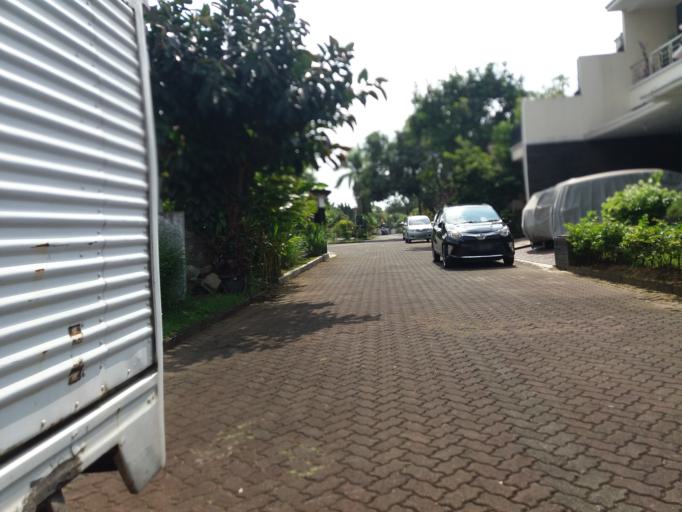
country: ID
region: West Java
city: Bandung
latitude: -6.9165
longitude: 107.6537
